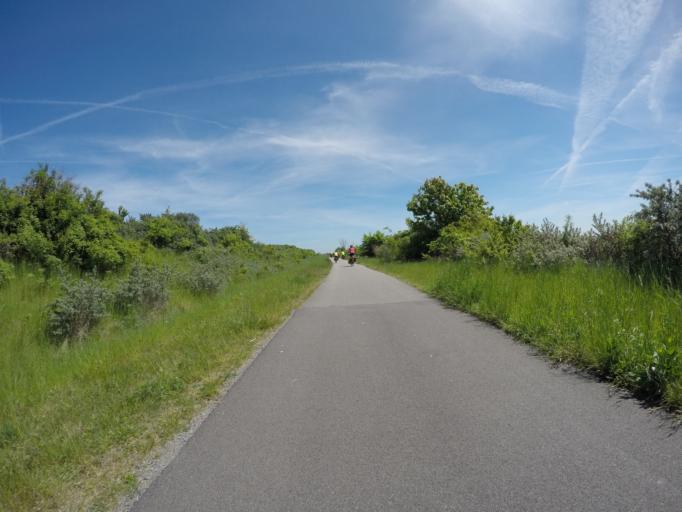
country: SE
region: Skane
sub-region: Malmo
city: Bunkeflostrand
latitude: 55.5632
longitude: 12.9036
